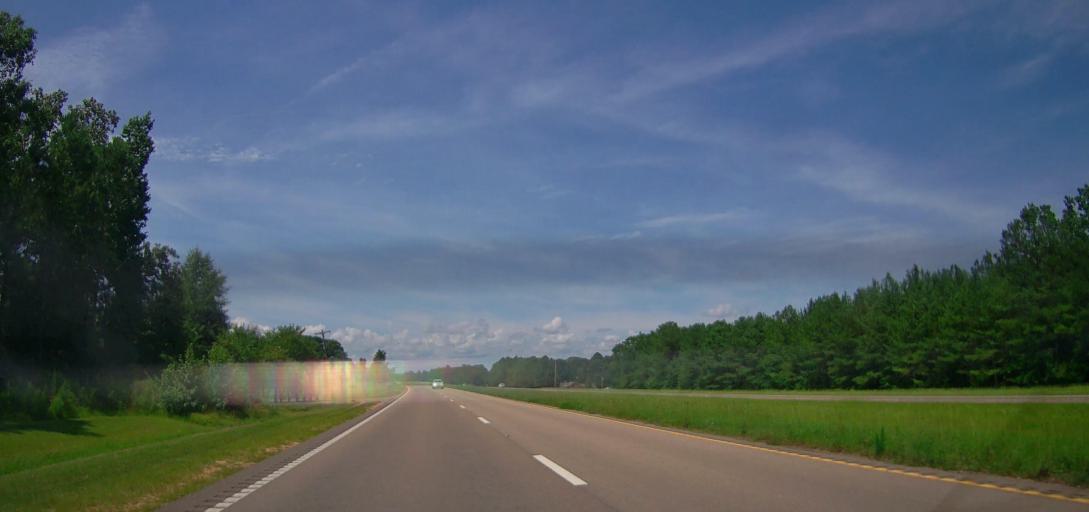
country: US
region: Mississippi
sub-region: Monroe County
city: Aberdeen
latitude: 33.9276
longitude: -88.5962
